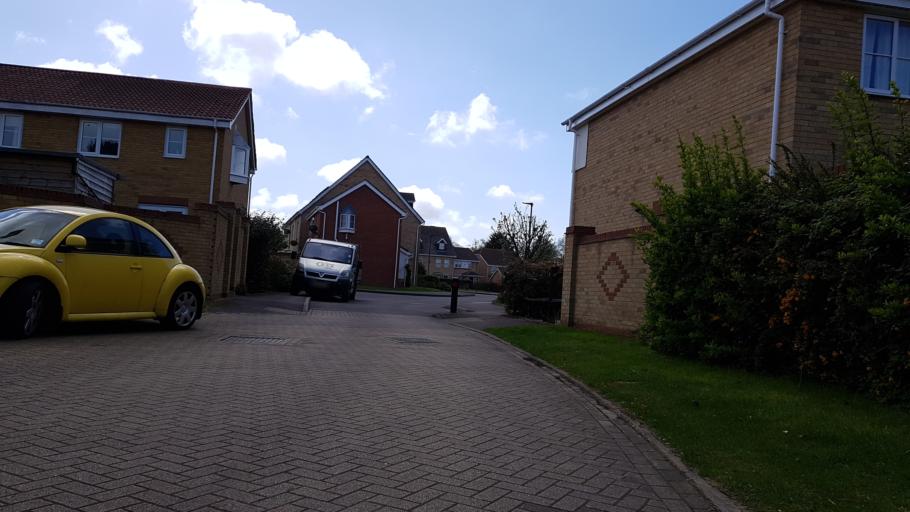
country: GB
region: England
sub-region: Isle of Wight
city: East Cowes
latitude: 50.7578
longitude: -1.2775
